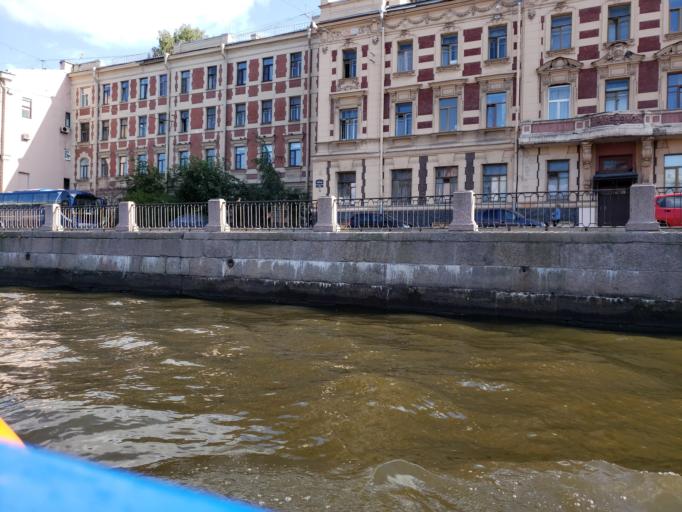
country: RU
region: St.-Petersburg
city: Saint Petersburg
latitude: 59.9234
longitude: 30.3228
